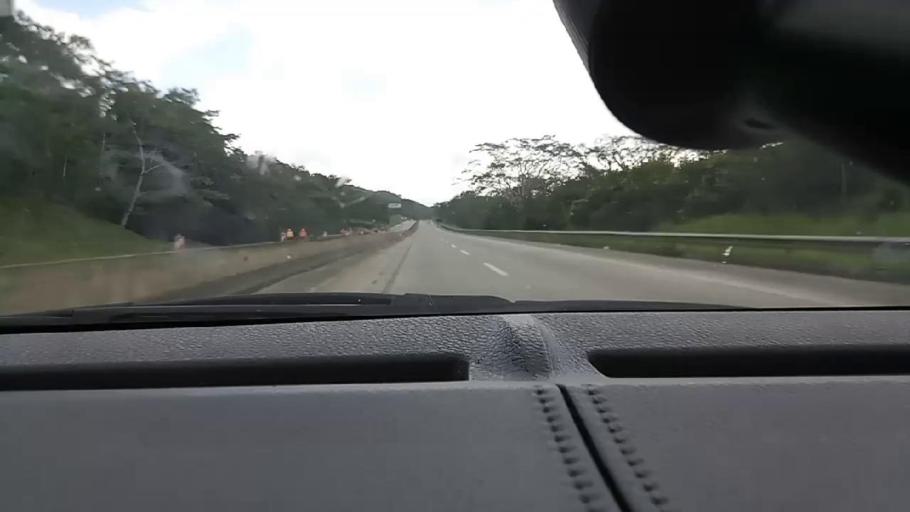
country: PA
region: Panama
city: Chilibre
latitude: 9.1562
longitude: -79.6370
